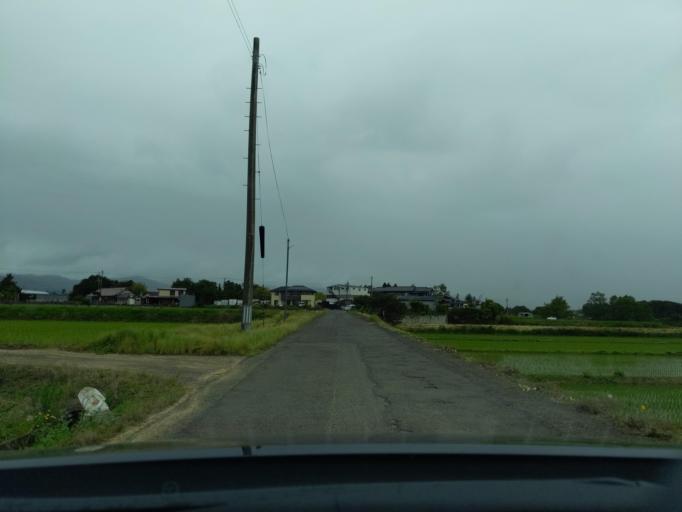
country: JP
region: Fukushima
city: Koriyama
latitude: 37.3678
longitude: 140.3082
